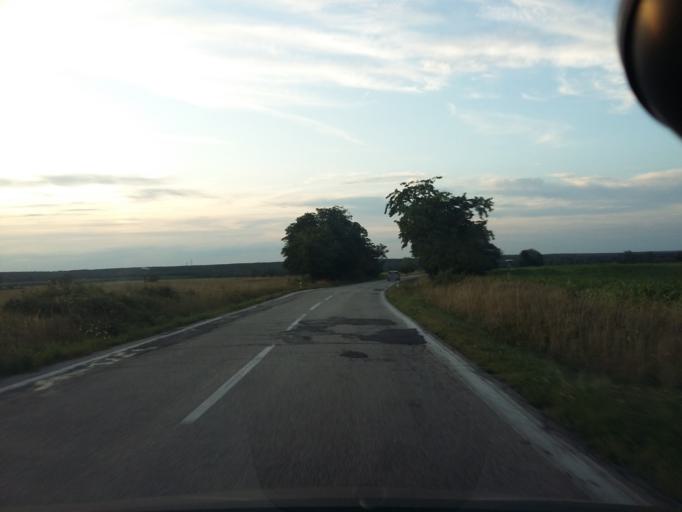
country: SK
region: Bratislavsky
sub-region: Okres Malacky
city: Malacky
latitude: 48.4383
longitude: 17.1588
